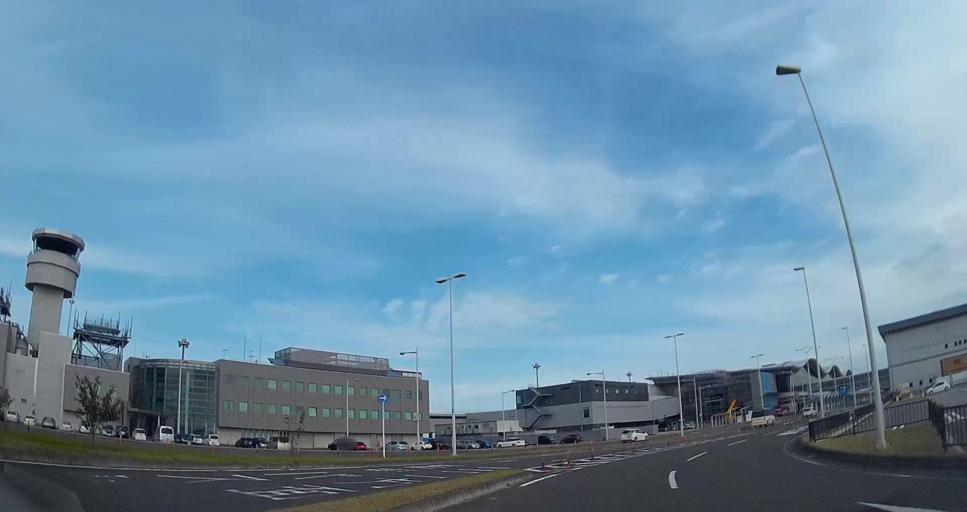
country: JP
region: Miyagi
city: Iwanuma
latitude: 38.1371
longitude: 140.9268
